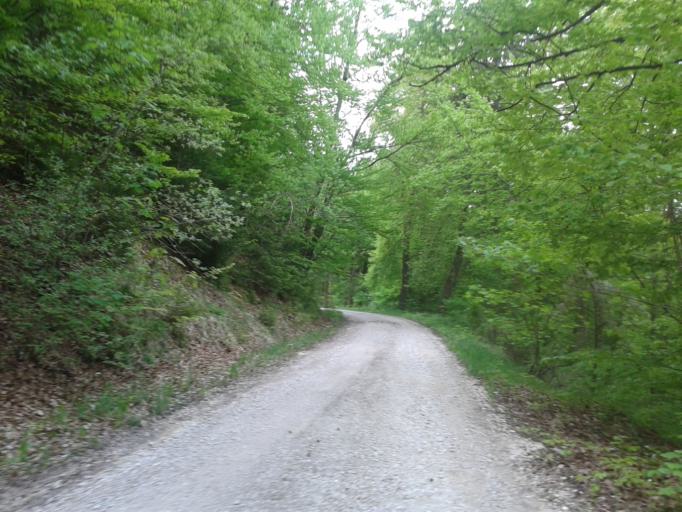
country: DE
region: Baden-Wuerttemberg
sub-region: Tuebingen Region
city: Blaubeuren
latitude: 48.4010
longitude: 9.7918
